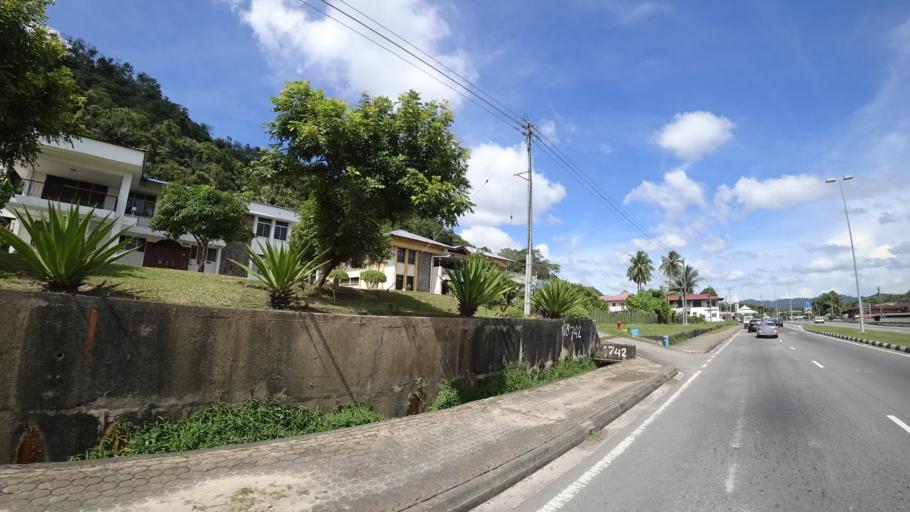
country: BN
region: Brunei and Muara
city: Bandar Seri Begawan
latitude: 4.8525
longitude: 114.8822
